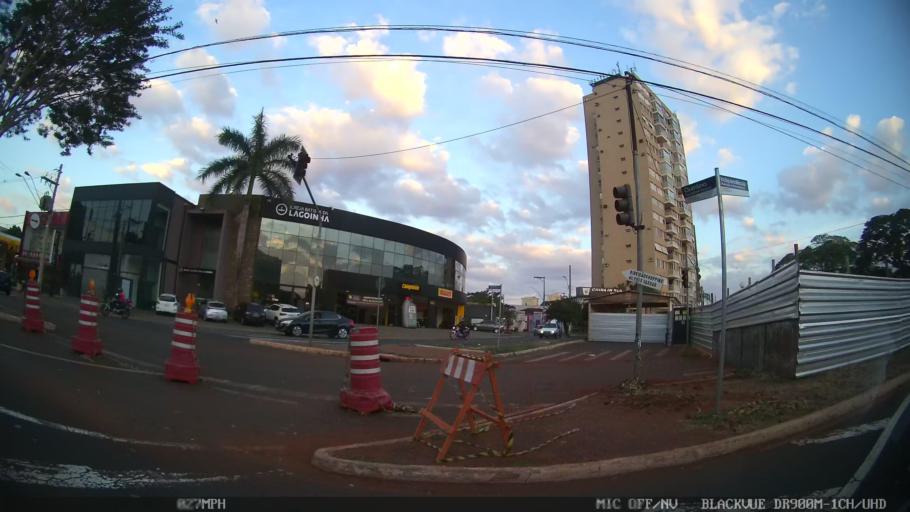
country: BR
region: Sao Paulo
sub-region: Ribeirao Preto
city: Ribeirao Preto
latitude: -21.1874
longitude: -47.8066
